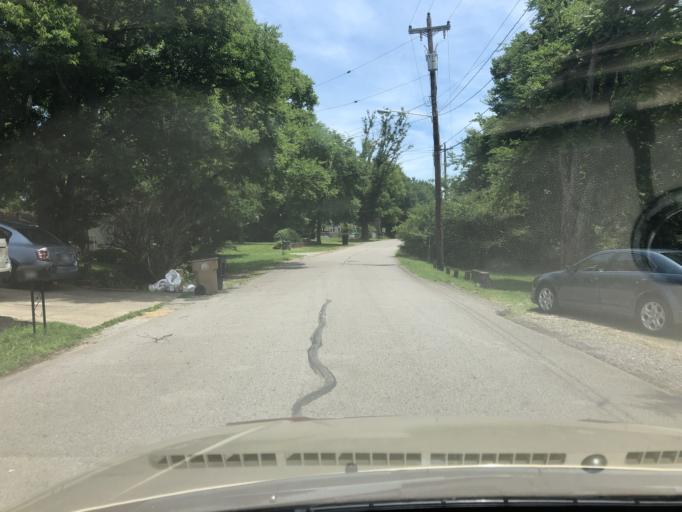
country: US
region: Tennessee
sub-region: Davidson County
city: Lakewood
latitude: 36.2525
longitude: -86.7055
